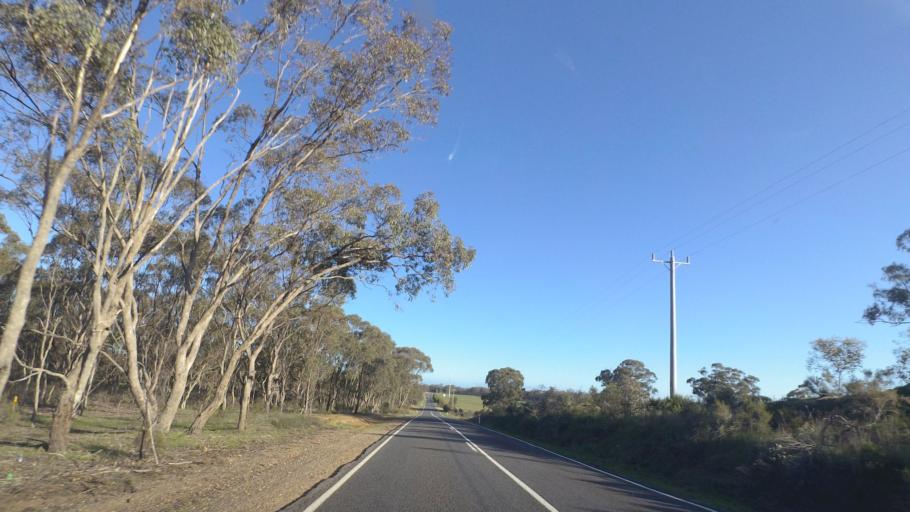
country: AU
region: Victoria
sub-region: Greater Bendigo
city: Kennington
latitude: -36.8655
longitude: 144.5013
